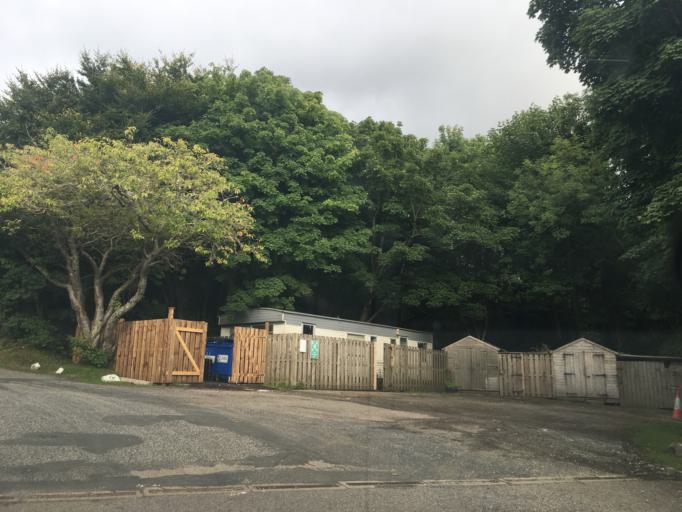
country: GB
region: Scotland
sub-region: Argyll and Bute
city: Oban
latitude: 56.2352
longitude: -5.5535
